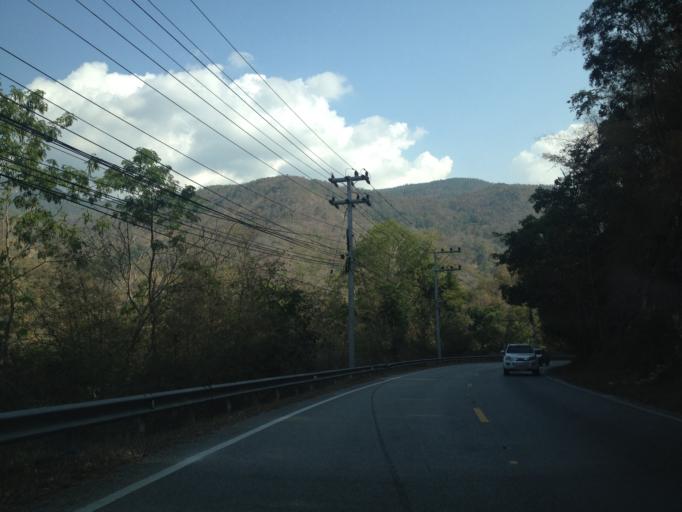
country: TH
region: Chiang Mai
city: Hot
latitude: 18.2263
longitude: 98.4482
